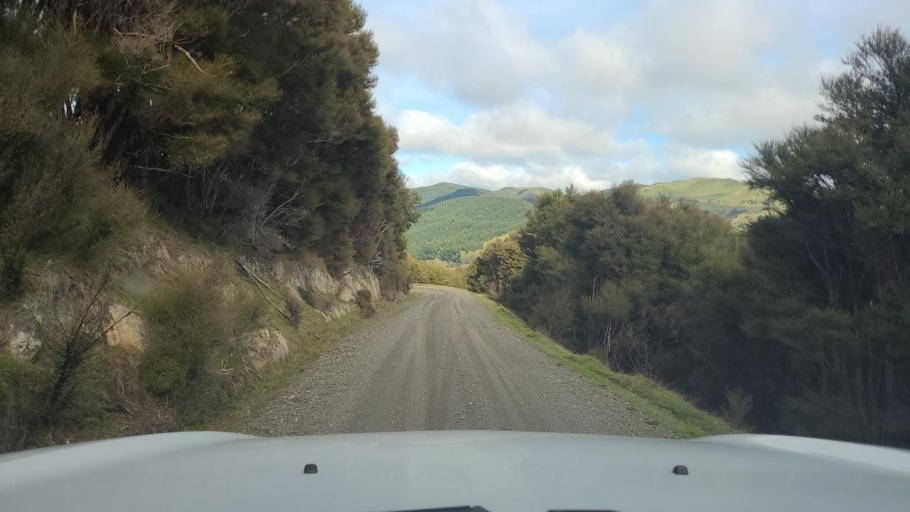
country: NZ
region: Wellington
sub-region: South Wairarapa District
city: Waipawa
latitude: -41.2576
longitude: 175.6891
